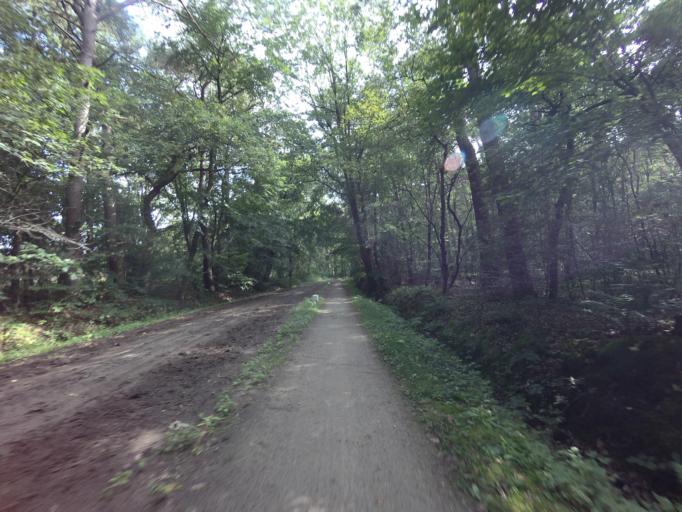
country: NL
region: Overijssel
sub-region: Gemeente Hengelo
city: Hengelo
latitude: 52.2599
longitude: 6.8496
